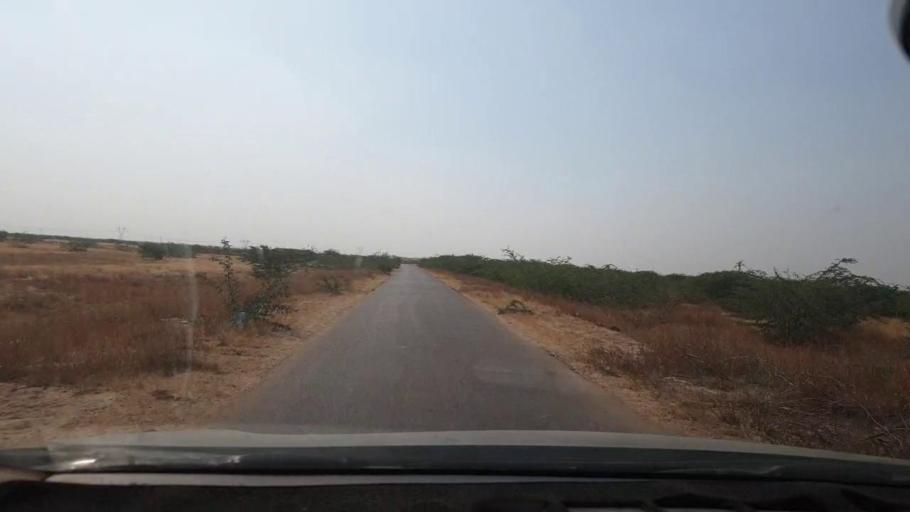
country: PK
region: Sindh
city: Malir Cantonment
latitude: 25.1259
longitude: 67.2236
